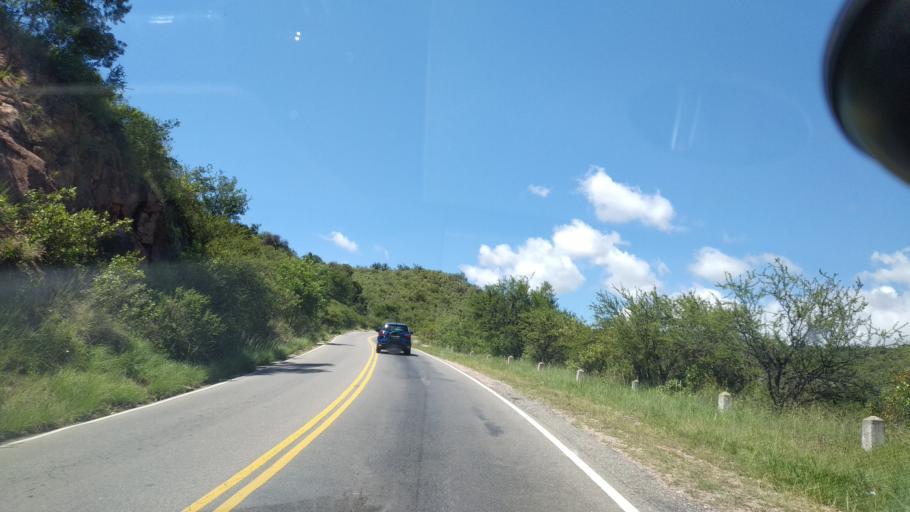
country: AR
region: Cordoba
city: Villa Cura Brochero
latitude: -31.6945
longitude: -65.0517
